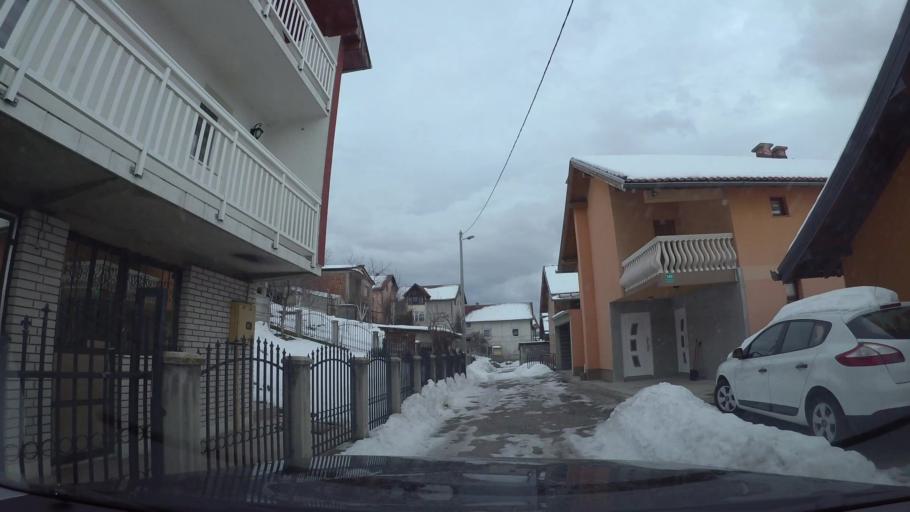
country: BA
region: Federation of Bosnia and Herzegovina
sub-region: Kanton Sarajevo
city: Sarajevo
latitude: 43.8651
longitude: 18.3617
